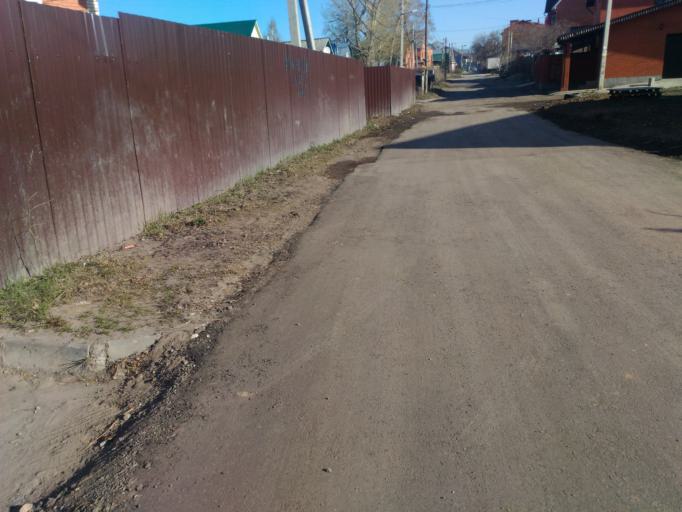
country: RU
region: Ulyanovsk
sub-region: Ulyanovskiy Rayon
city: Ulyanovsk
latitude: 54.3374
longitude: 48.3892
